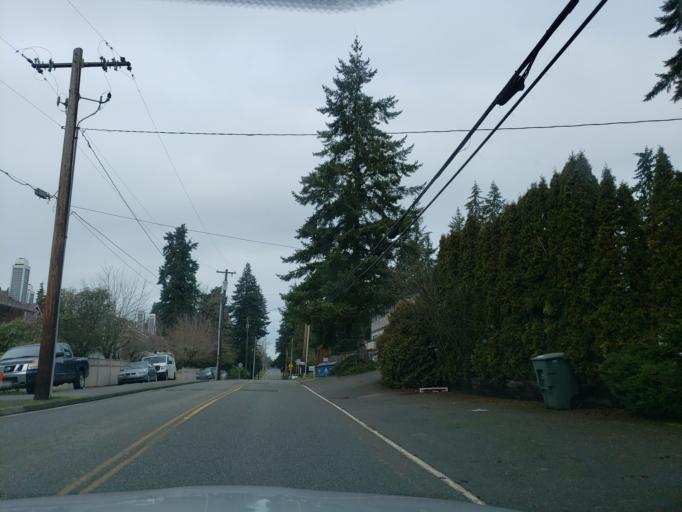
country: US
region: Washington
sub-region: Snohomish County
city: Lynnwood
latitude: 47.8217
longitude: -122.3414
